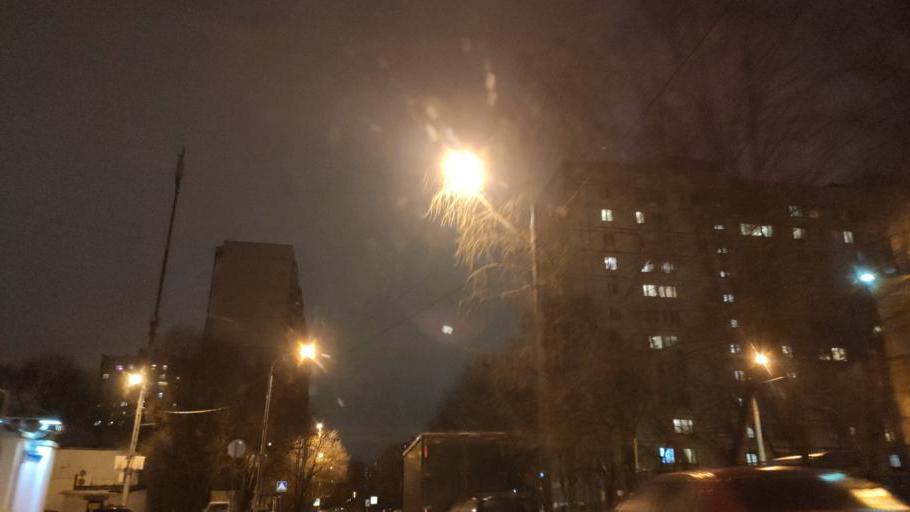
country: RU
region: Moscow
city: Kotlovka
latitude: 55.6624
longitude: 37.6068
